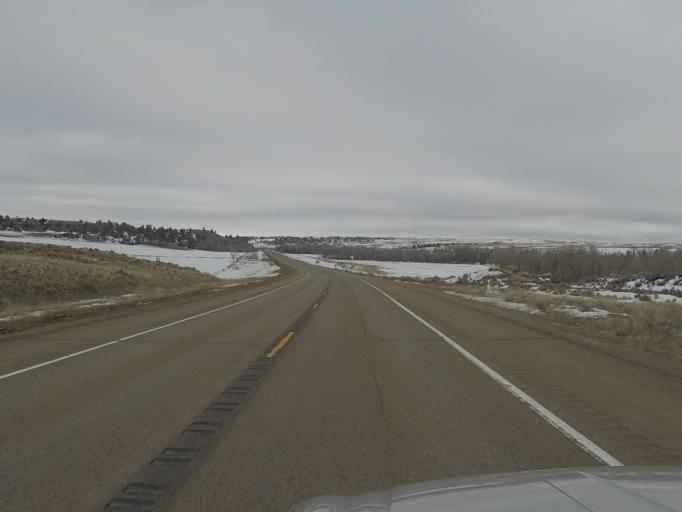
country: US
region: Montana
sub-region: Golden Valley County
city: Ryegate
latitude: 46.3107
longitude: -109.1267
